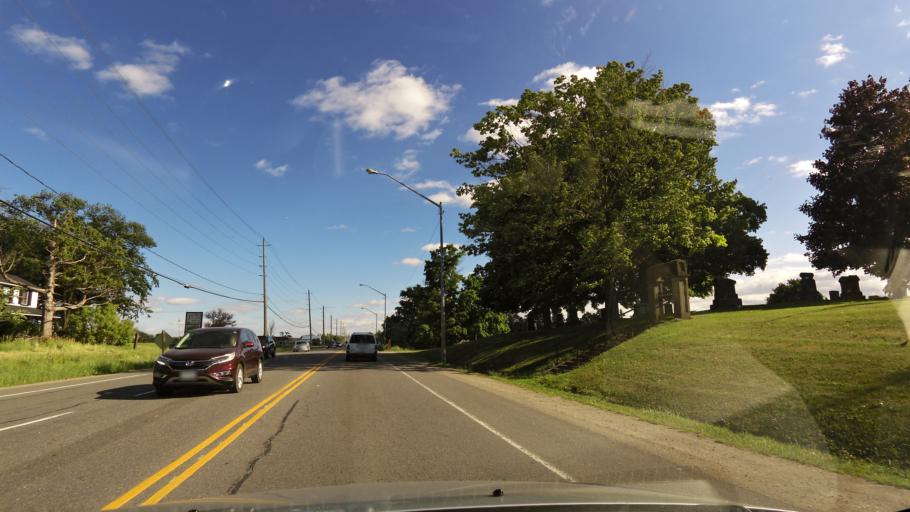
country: CA
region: Ontario
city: Bradford West Gwillimbury
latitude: 44.0035
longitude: -79.6768
